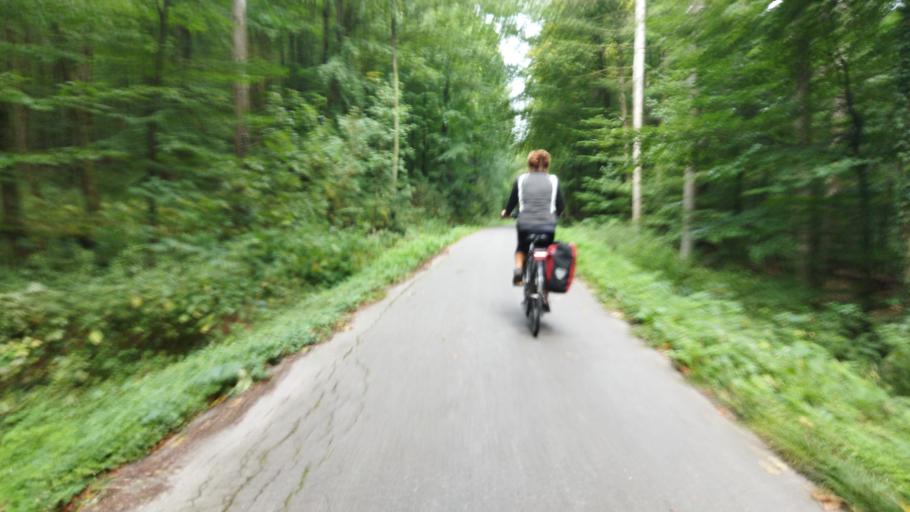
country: DE
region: Lower Saxony
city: Bad Iburg
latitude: 52.1585
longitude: 8.0770
